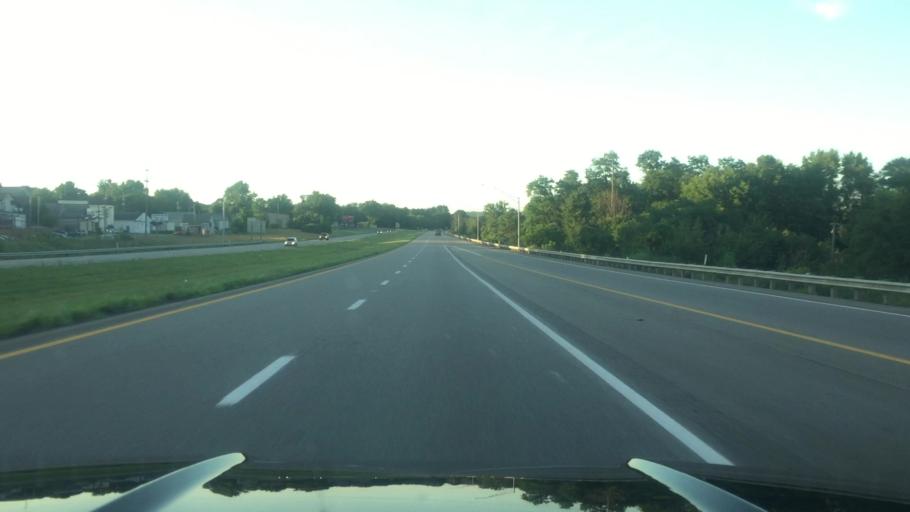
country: US
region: Ohio
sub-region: Tuscarawas County
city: Strasburg
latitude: 40.6467
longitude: -81.4508
